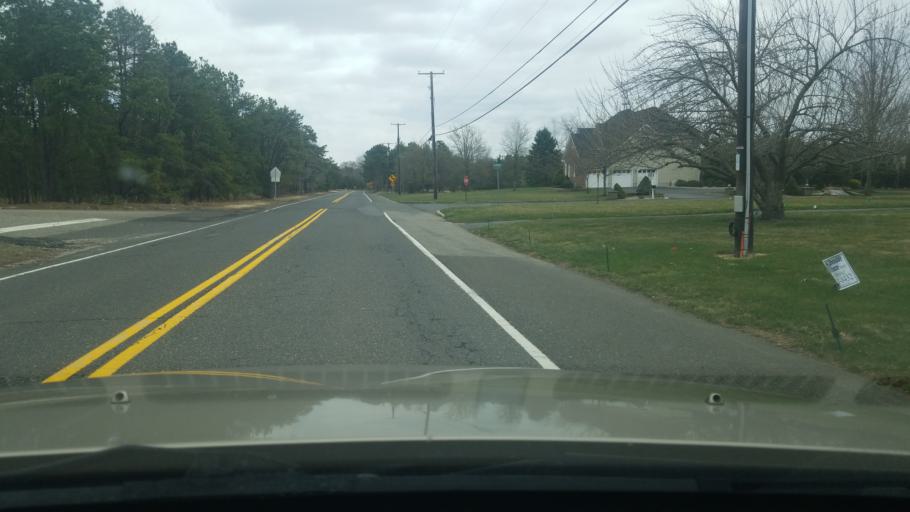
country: US
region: New Jersey
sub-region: Monmouth County
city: Ramtown
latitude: 40.1353
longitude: -74.1271
